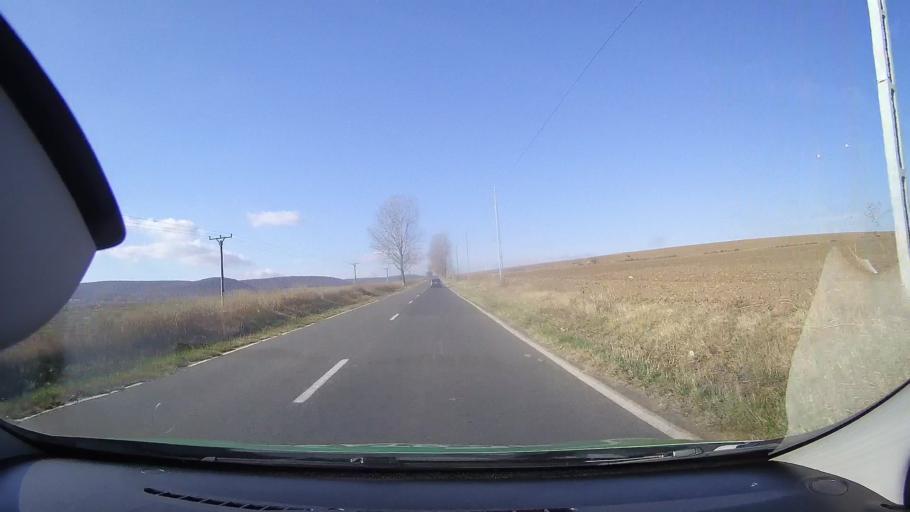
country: RO
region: Tulcea
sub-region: Comuna Sarichioi
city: Enisala
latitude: 44.8791
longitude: 28.7914
